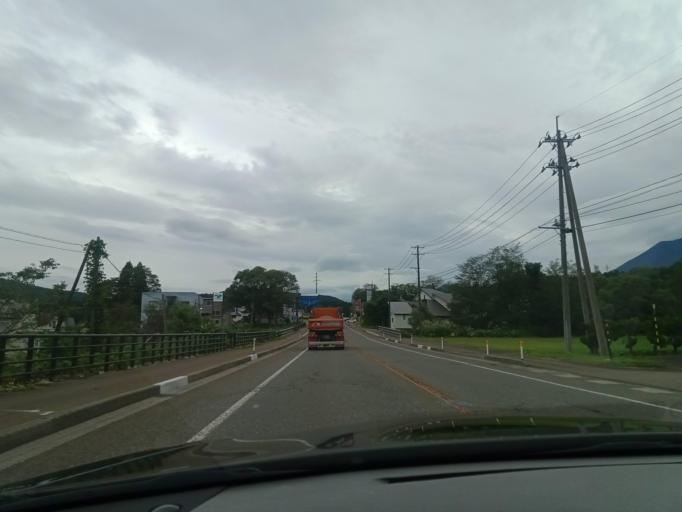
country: JP
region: Niigata
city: Arai
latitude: 36.8818
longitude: 138.2053
